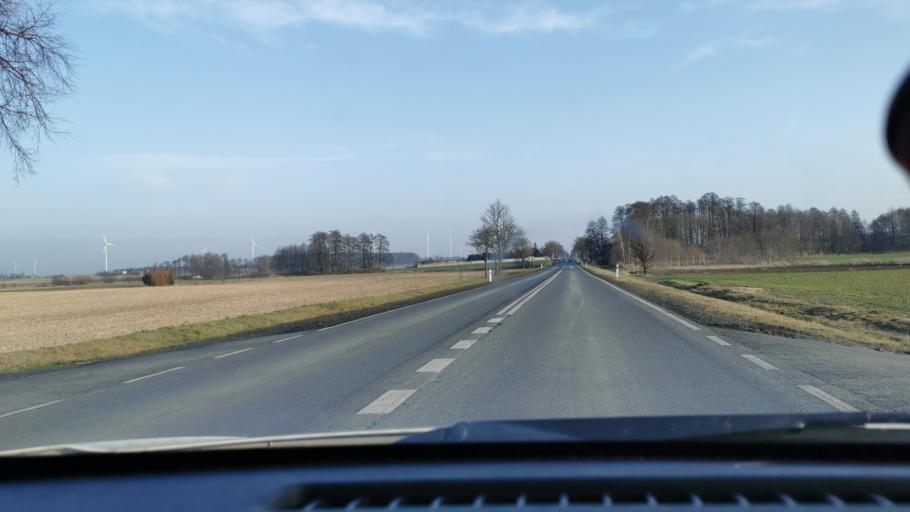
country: PL
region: Lodz Voivodeship
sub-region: Powiat sieradzki
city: Blaszki
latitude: 51.6419
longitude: 18.4935
